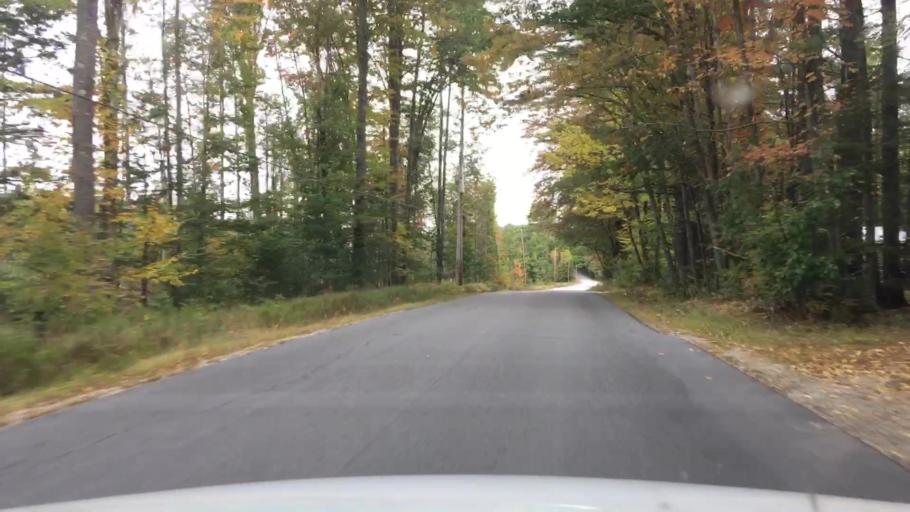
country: US
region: Maine
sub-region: Cumberland County
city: Harrison
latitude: 44.2492
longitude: -70.7216
